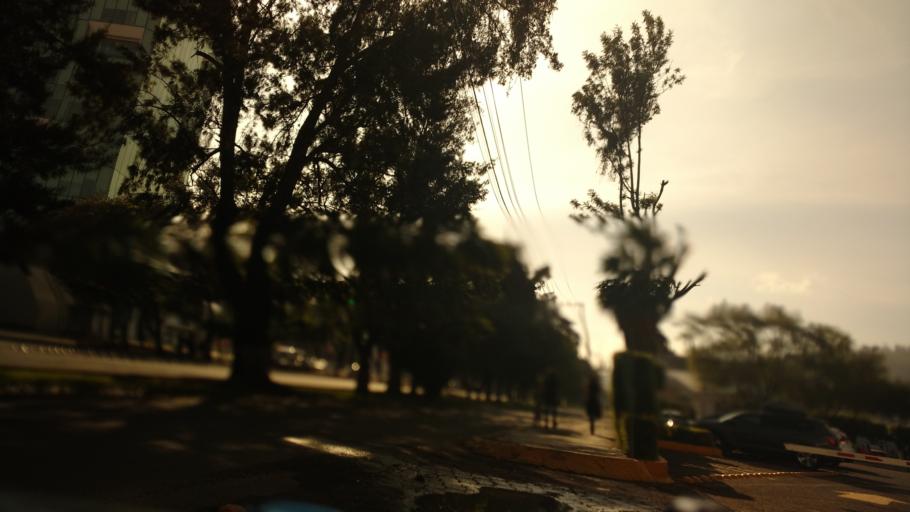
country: MX
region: Michoacan
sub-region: Morelia
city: Montana Monarca (Punta Altozano)
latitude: 19.6874
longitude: -101.1567
